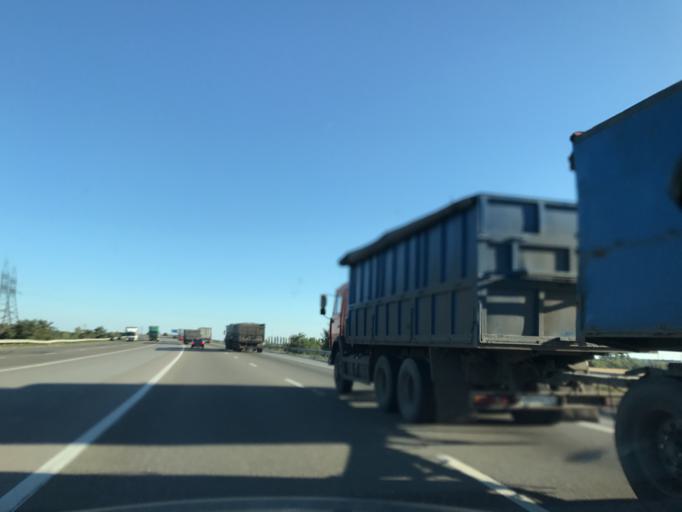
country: RU
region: Rostov
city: Likhoy
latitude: 48.0393
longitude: 40.2587
